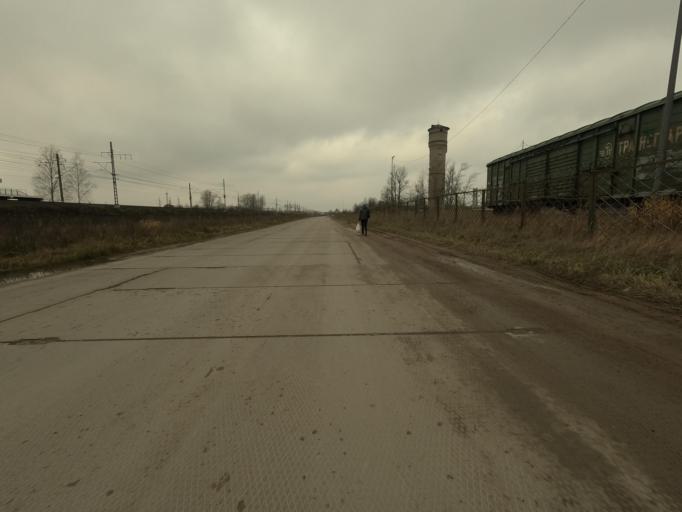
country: RU
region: Leningrad
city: Lyuban'
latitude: 59.4708
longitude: 31.2538
